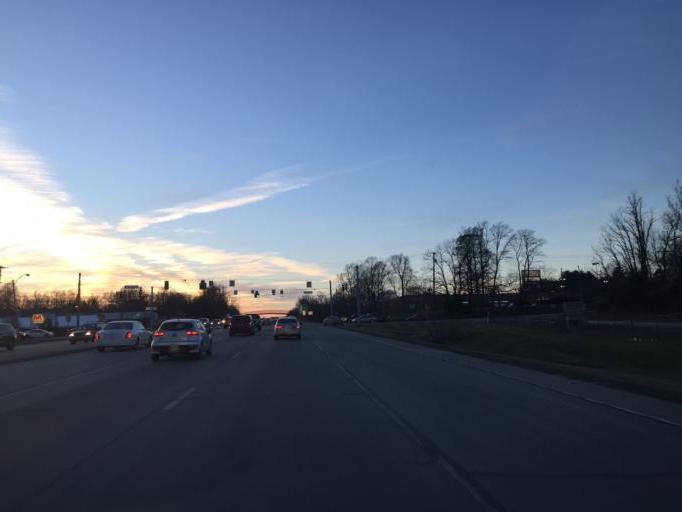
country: US
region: Indiana
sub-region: Monroe County
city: Bloomington
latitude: 39.1865
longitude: -86.5365
